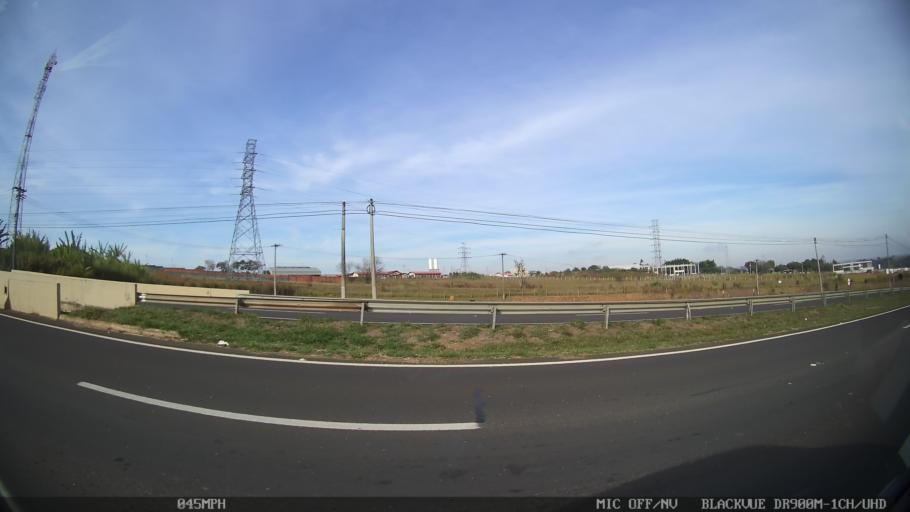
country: BR
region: Sao Paulo
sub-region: Piracicaba
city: Piracicaba
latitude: -22.6786
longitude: -47.7143
